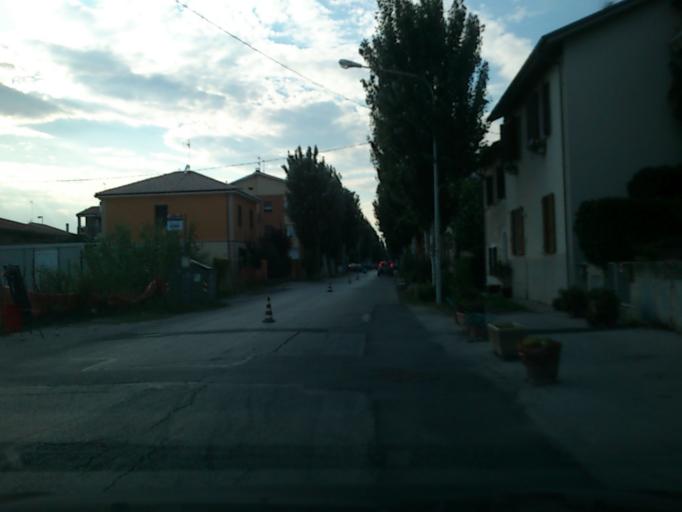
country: IT
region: The Marches
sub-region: Provincia di Pesaro e Urbino
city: Fano
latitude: 43.8435
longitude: 13.0287
